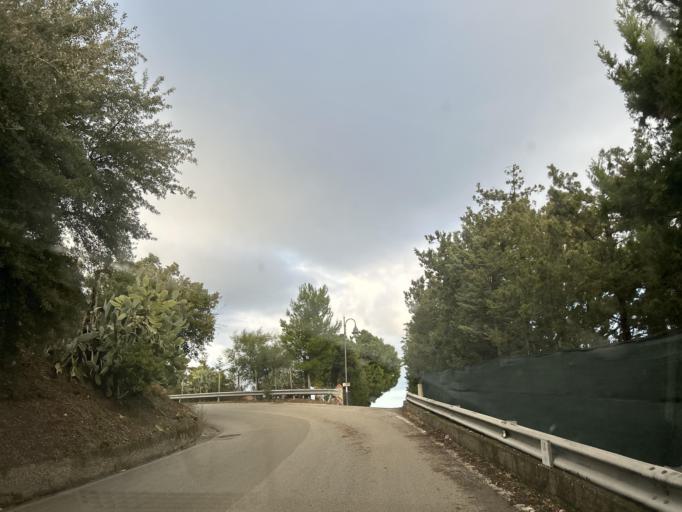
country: IT
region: Calabria
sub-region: Provincia di Catanzaro
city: Squillace Lido
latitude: 38.7585
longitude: 16.5656
